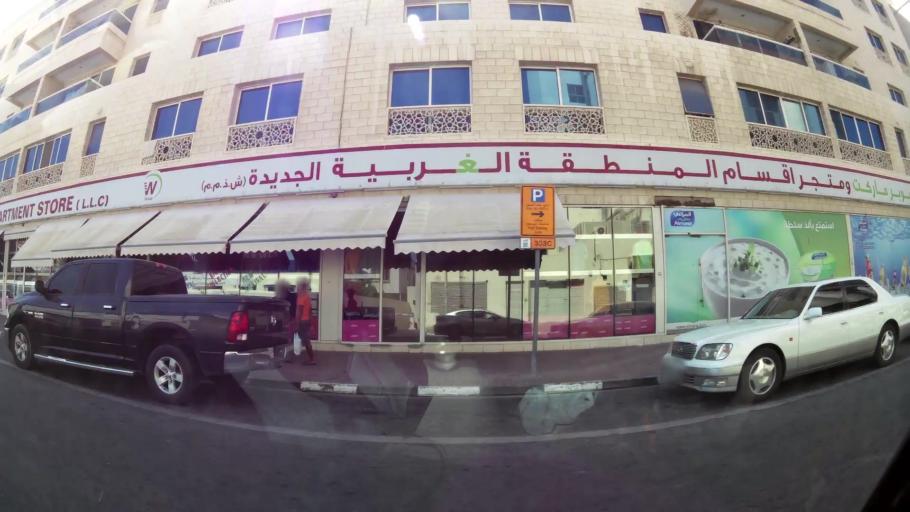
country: AE
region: Ash Shariqah
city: Sharjah
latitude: 25.2309
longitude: 55.2719
